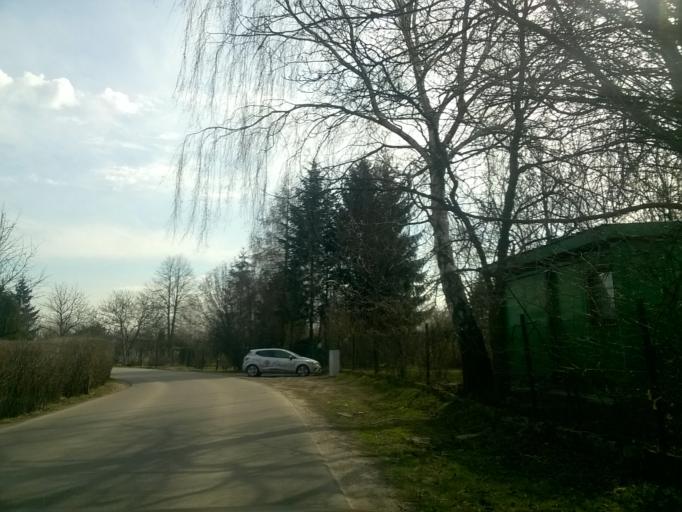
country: PL
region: Lesser Poland Voivodeship
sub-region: Powiat krakowski
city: Rzaska
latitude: 50.0892
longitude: 19.8633
